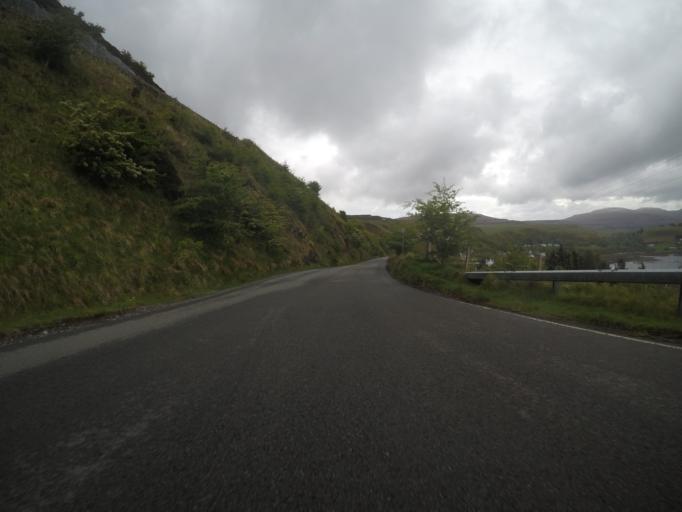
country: GB
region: Scotland
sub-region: Highland
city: Portree
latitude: 57.5910
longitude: -6.3781
